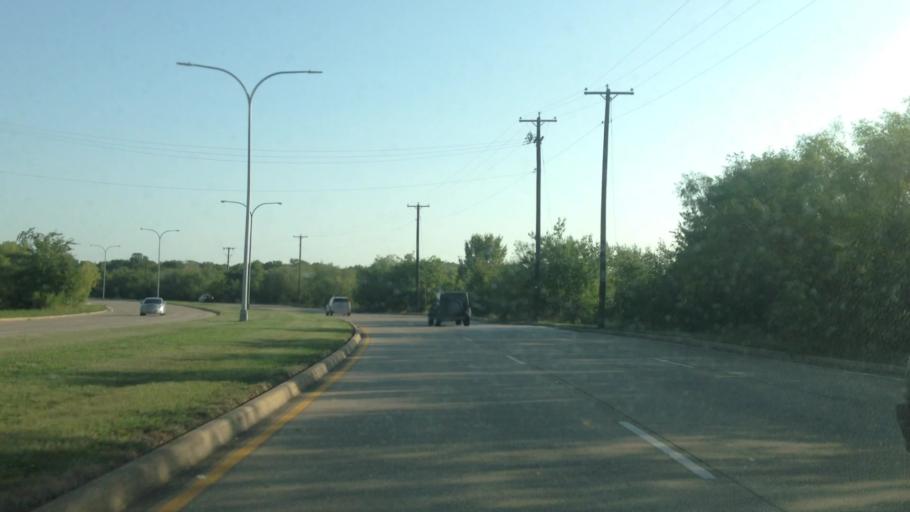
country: US
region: Texas
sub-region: Tarrant County
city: Pantego
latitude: 32.7469
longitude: -97.1728
